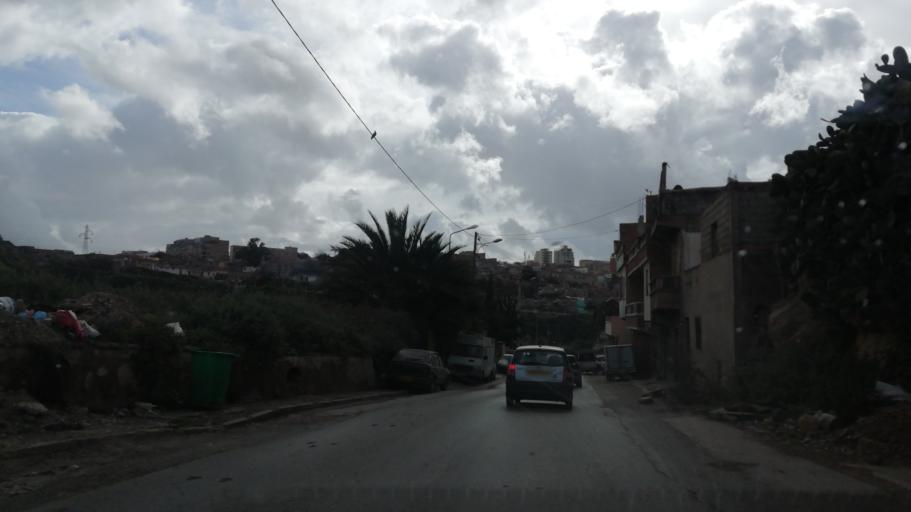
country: DZ
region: Oran
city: Oran
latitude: 35.6959
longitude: -0.6592
